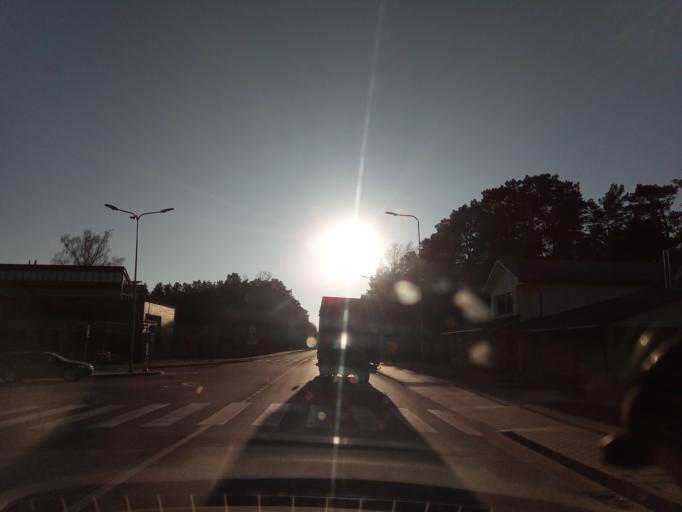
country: LT
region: Alytaus apskritis
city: Druskininkai
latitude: 54.0209
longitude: 24.0010
